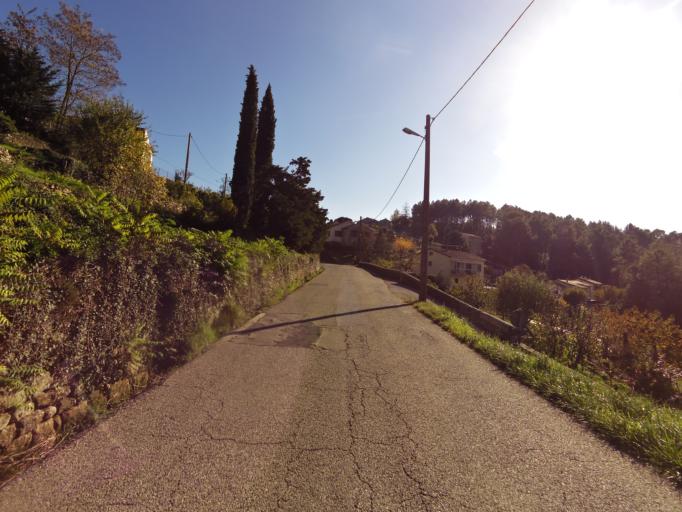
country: FR
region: Rhone-Alpes
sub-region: Departement de l'Ardeche
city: Largentiere
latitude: 44.5434
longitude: 4.2975
